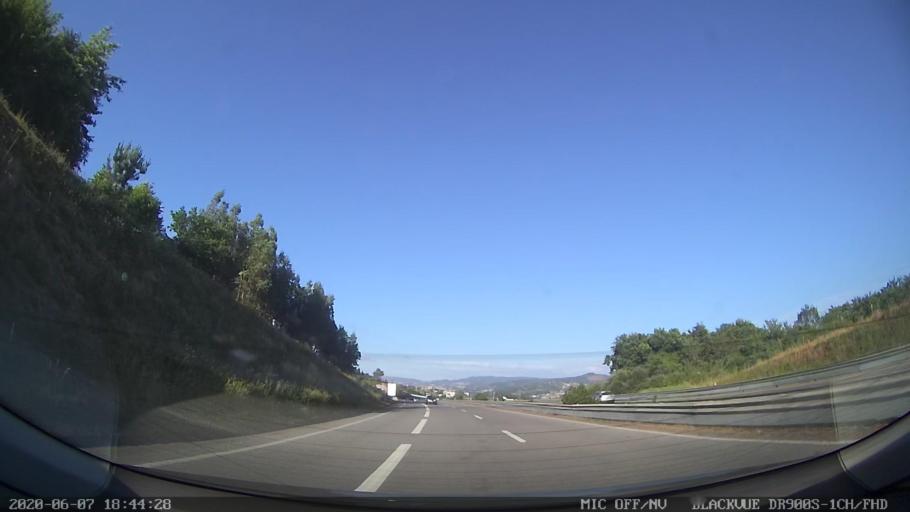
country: PT
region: Braga
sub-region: Vila Nova de Famalicao
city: Joane
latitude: 41.4068
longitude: -8.4156
